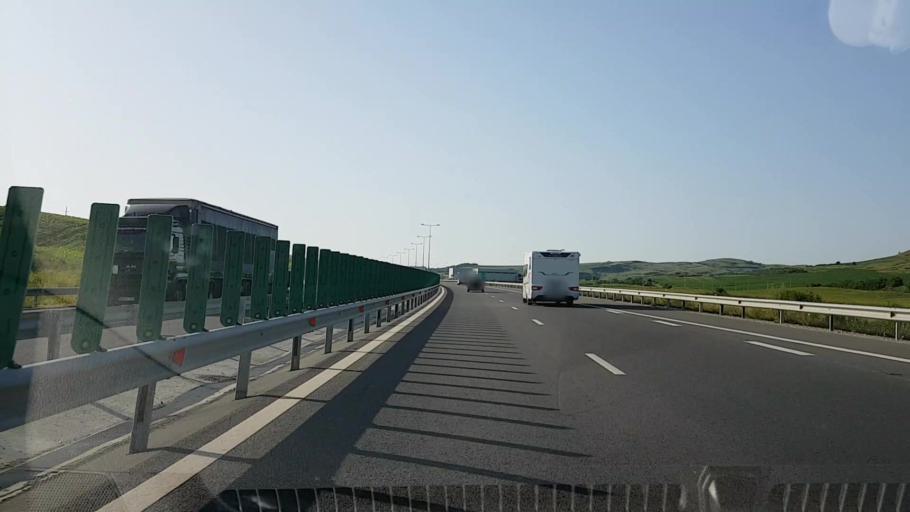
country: RO
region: Alba
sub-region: Comuna Unirea
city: Unirea
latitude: 46.4462
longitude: 23.7969
